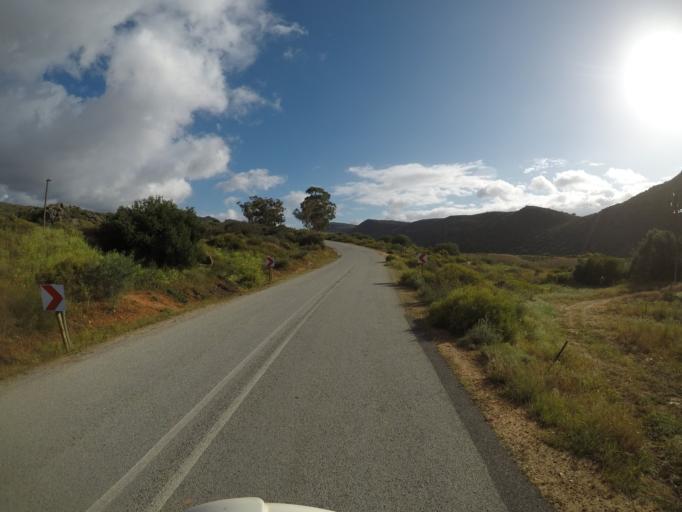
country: ZA
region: Western Cape
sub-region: West Coast District Municipality
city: Clanwilliam
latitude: -32.4335
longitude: 18.9394
